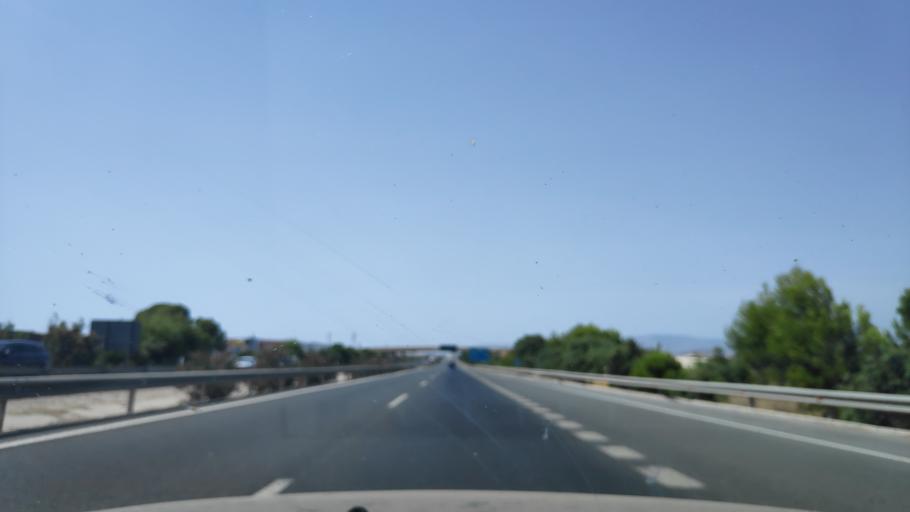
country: ES
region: Murcia
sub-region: Murcia
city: Lorqui
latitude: 38.0870
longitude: -1.2231
